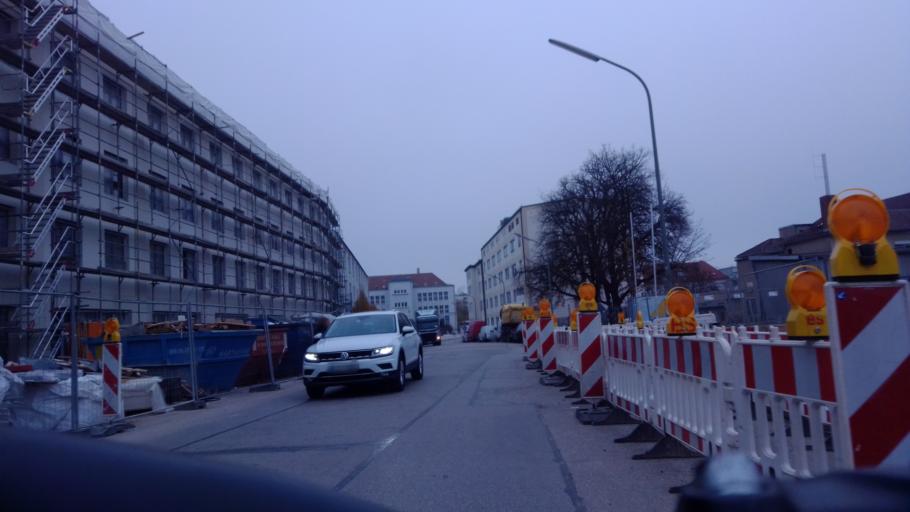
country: DE
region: Bavaria
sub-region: Upper Bavaria
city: Pullach im Isartal
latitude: 48.1022
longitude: 11.5382
